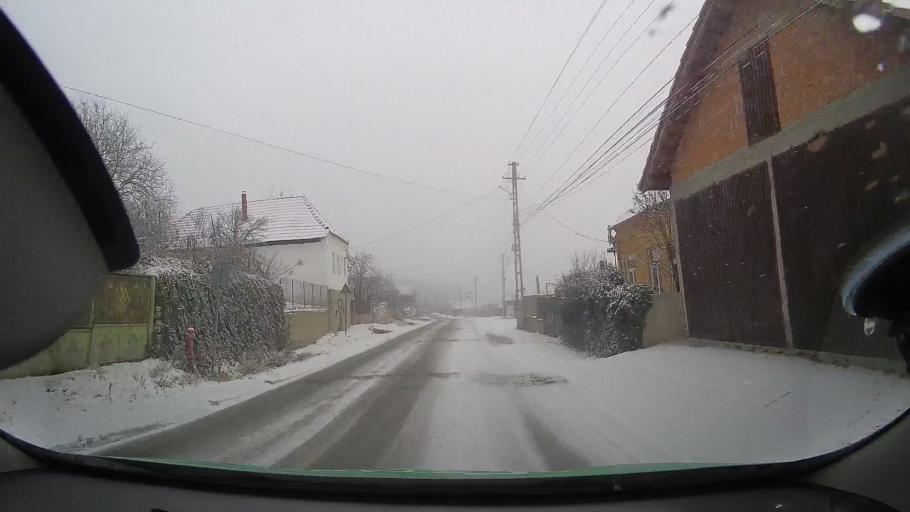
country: RO
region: Alba
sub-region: Comuna Livezile
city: Livezile
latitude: 46.3467
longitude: 23.6469
